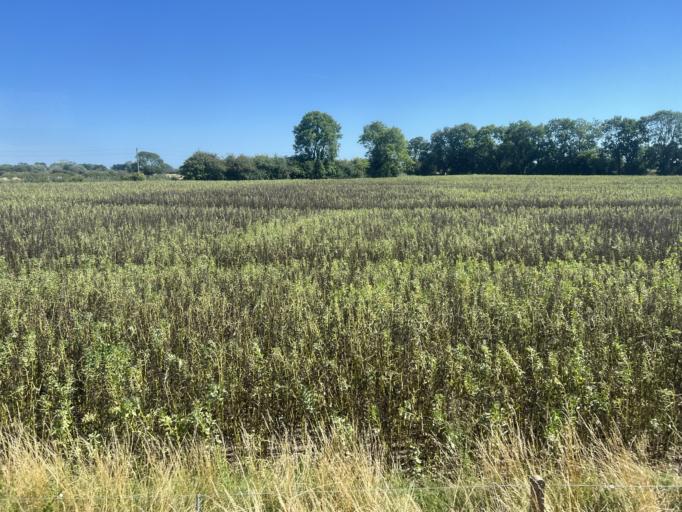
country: GB
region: England
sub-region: Lincolnshire
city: Wainfleet All Saints
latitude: 53.1313
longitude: 0.1927
